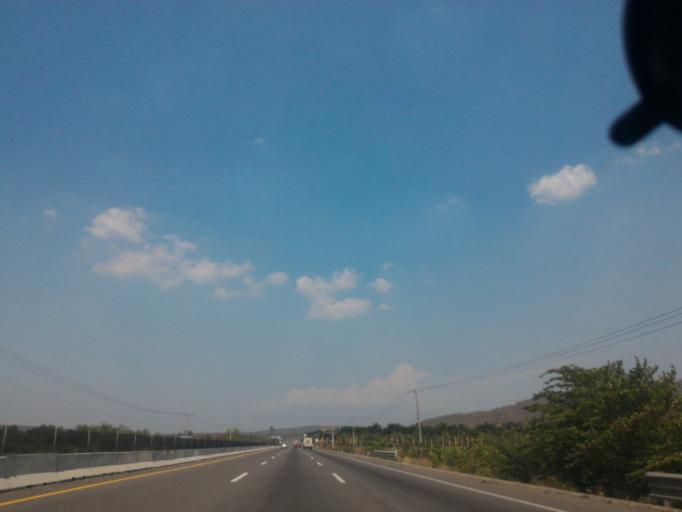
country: MX
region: Colima
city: Coquimatlan
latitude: 19.1437
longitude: -103.7705
